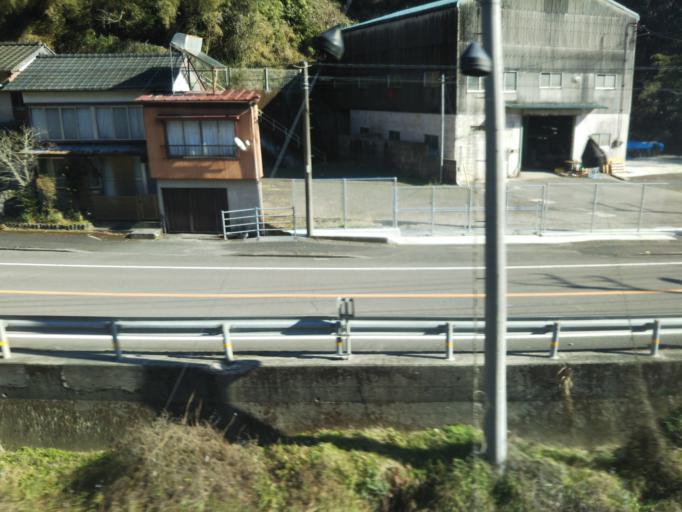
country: JP
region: Kochi
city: Nakamura
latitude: 33.1077
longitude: 133.0988
